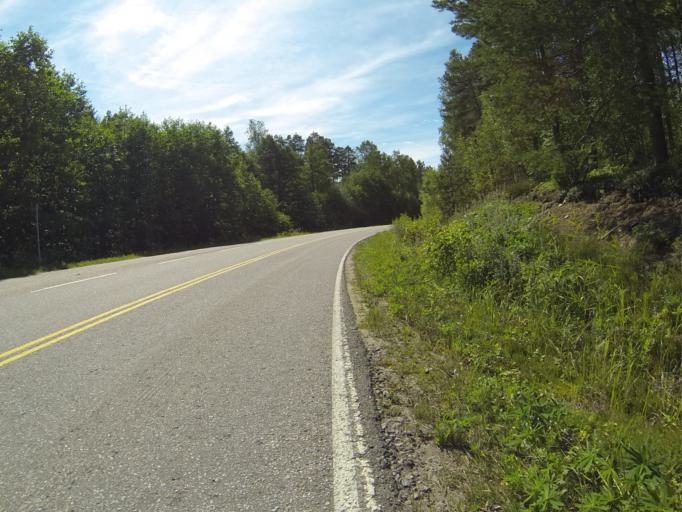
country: FI
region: Varsinais-Suomi
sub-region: Salo
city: Saerkisalo
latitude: 60.2644
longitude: 22.9737
